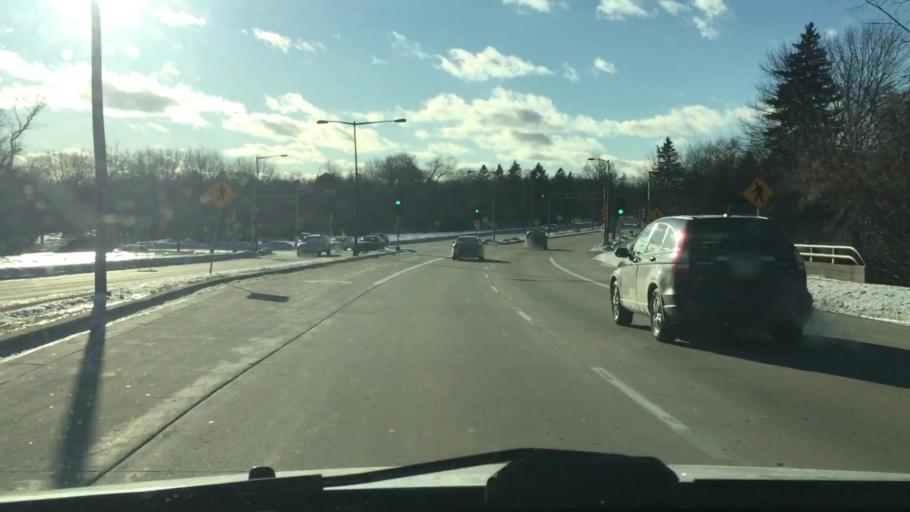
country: US
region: Wisconsin
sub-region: Milwaukee County
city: Hales Corners
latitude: 42.9885
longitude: -88.0571
